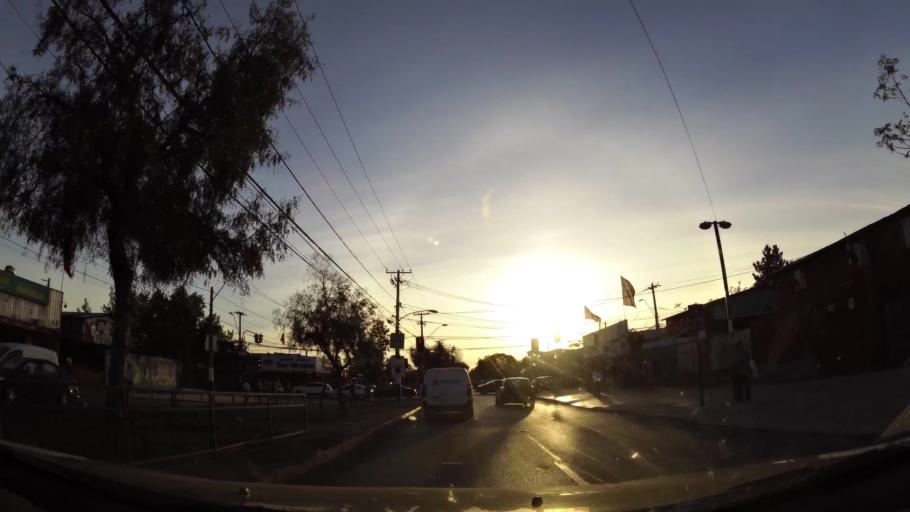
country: CL
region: Santiago Metropolitan
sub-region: Provincia de Cordillera
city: Puente Alto
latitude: -33.5970
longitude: -70.5658
